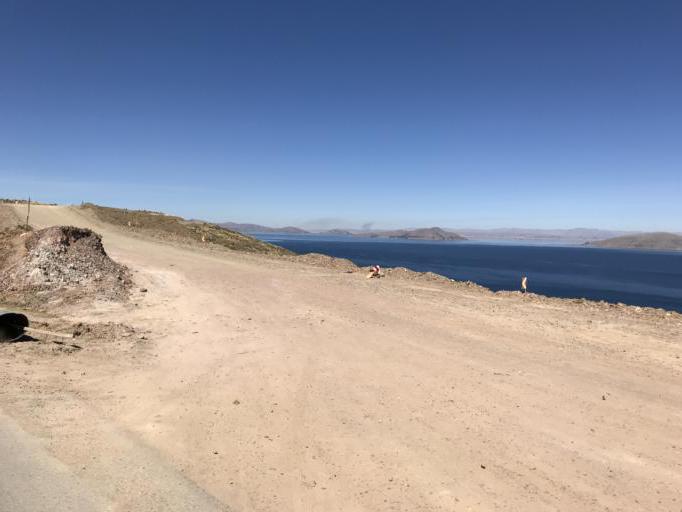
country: BO
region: La Paz
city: San Pablo
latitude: -16.1978
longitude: -68.8238
